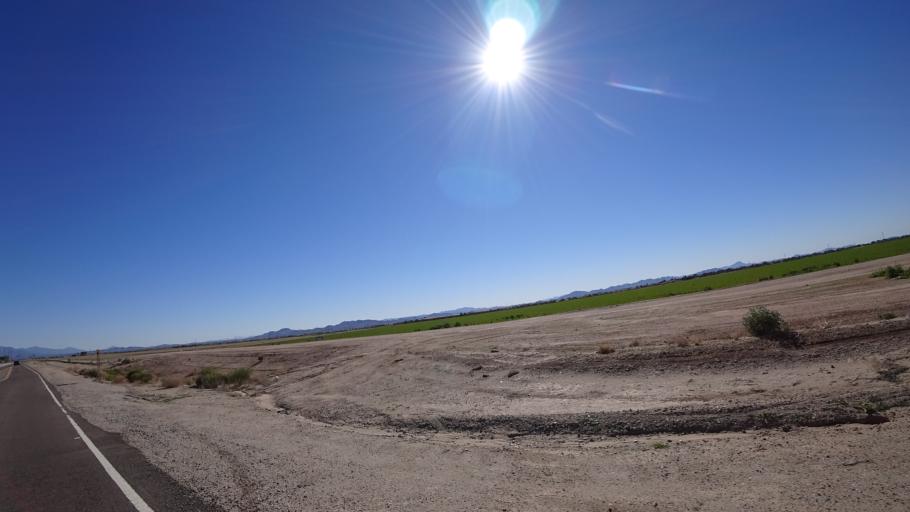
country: US
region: Arizona
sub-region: Maricopa County
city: Buckeye
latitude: 33.4206
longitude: -112.5835
